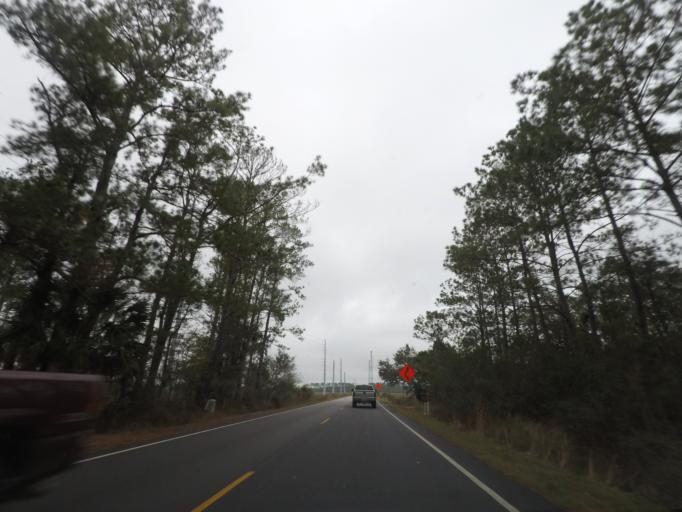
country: US
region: South Carolina
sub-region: Charleston County
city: Meggett
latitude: 32.6085
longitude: -80.3451
